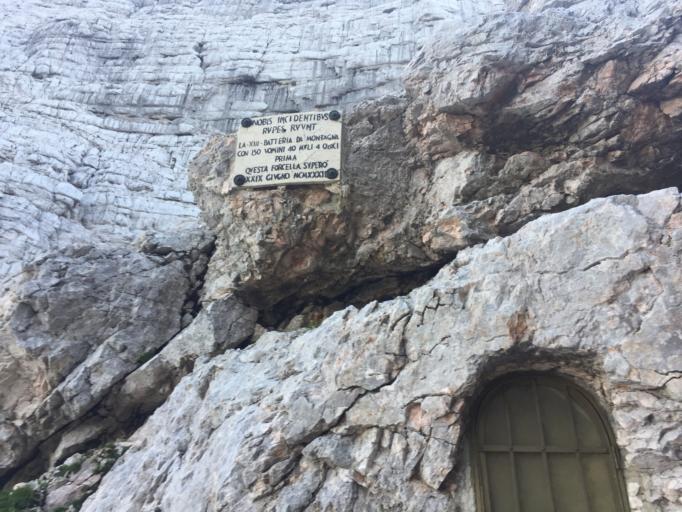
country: IT
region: Friuli Venezia Giulia
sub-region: Provincia di Udine
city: Malborghetto
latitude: 46.4184
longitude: 13.4808
